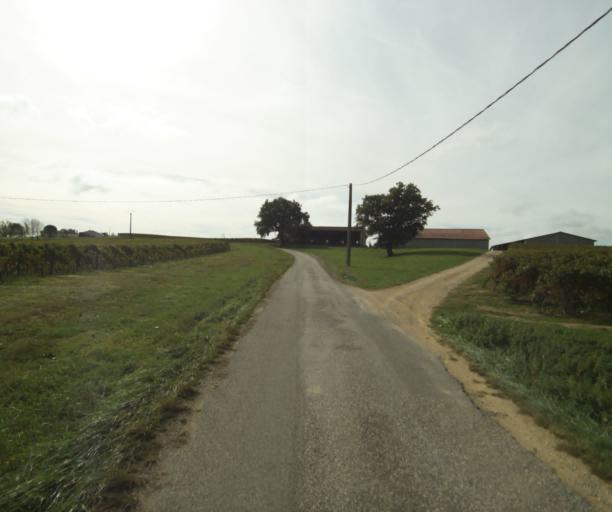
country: FR
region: Midi-Pyrenees
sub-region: Departement du Gers
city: Eauze
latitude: 43.8489
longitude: 0.1400
